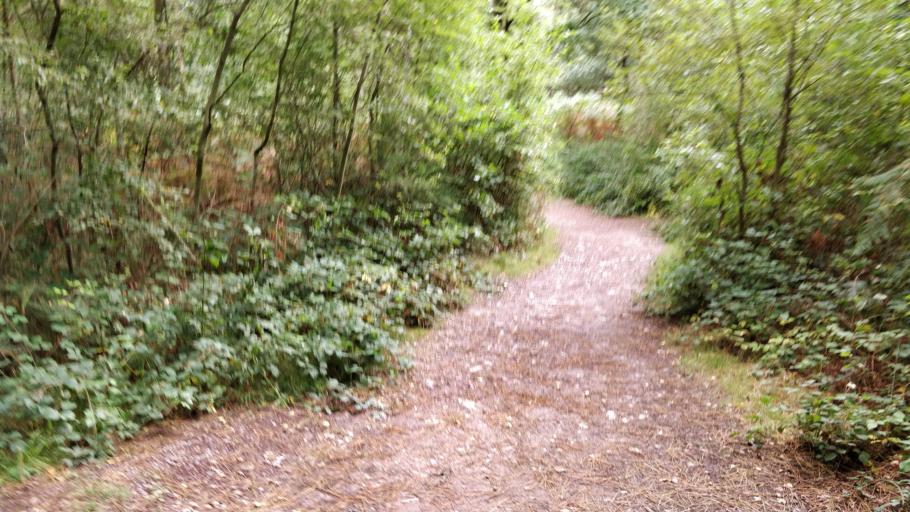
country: FR
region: Brittany
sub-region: Departement du Morbihan
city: Mauron
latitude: 48.0435
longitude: -2.2502
